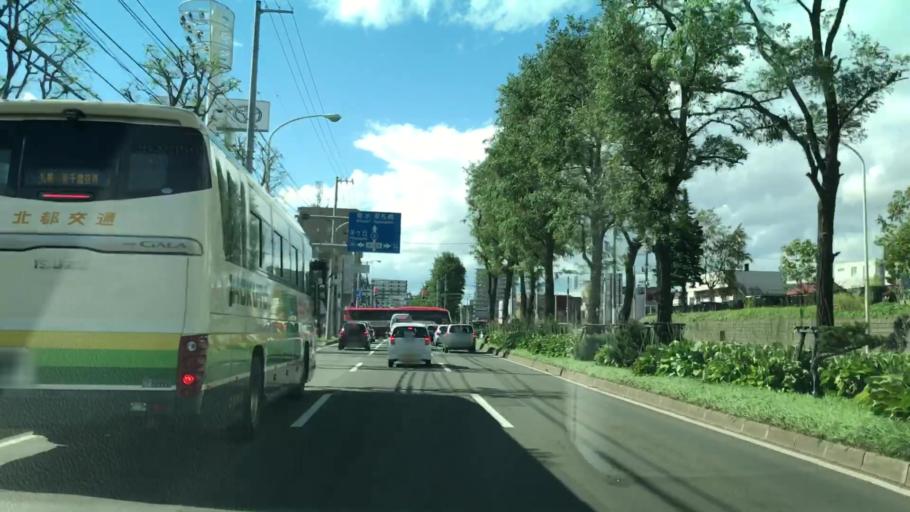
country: JP
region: Hokkaido
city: Sapporo
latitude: 43.0319
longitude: 141.4309
